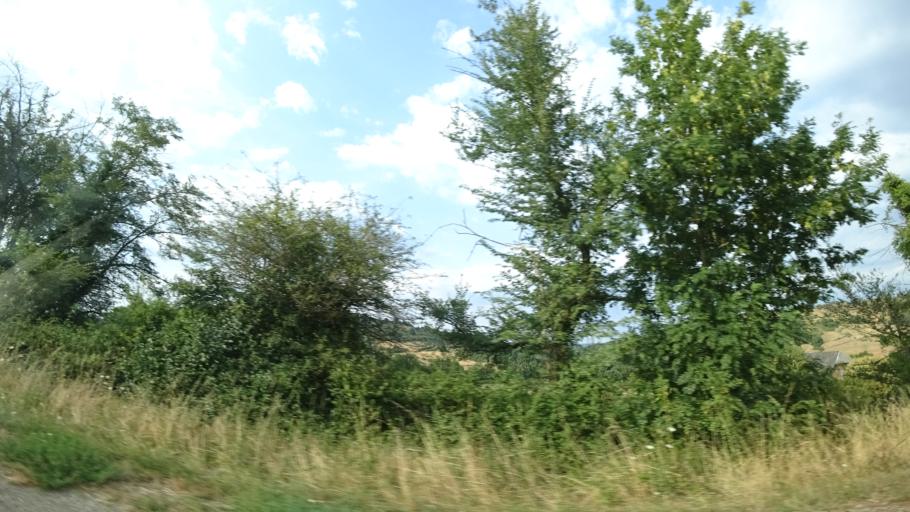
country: FR
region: Midi-Pyrenees
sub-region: Departement de l'Aveyron
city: Saint-Christophe-Vallon
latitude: 44.4961
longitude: 2.3846
